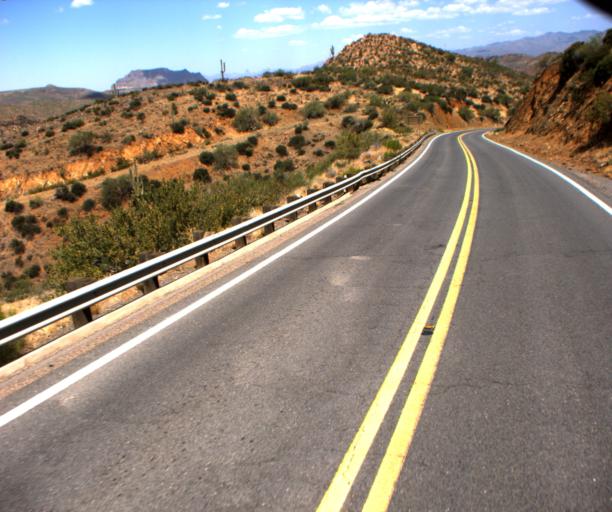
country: US
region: Arizona
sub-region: Pinal County
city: Superior
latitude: 33.2061
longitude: -111.0590
